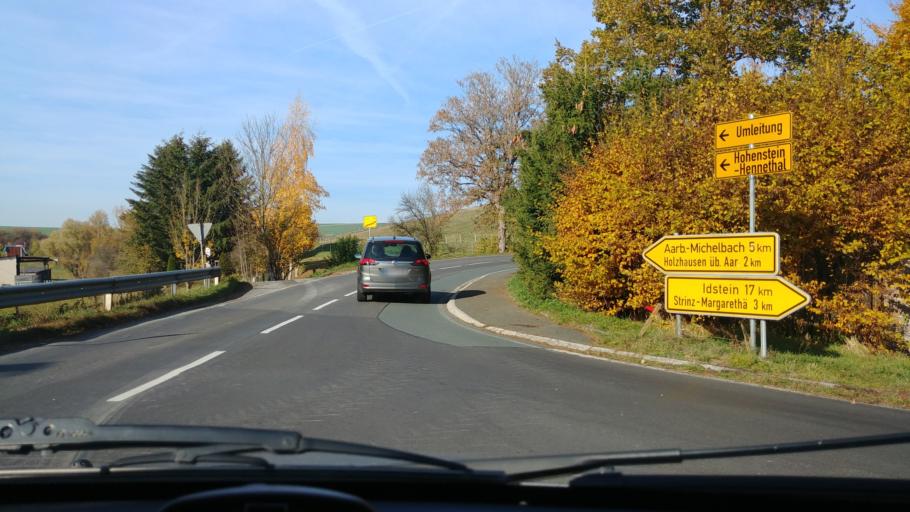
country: DE
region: Hesse
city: Burg Hohenstein
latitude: 50.1976
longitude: 8.0976
